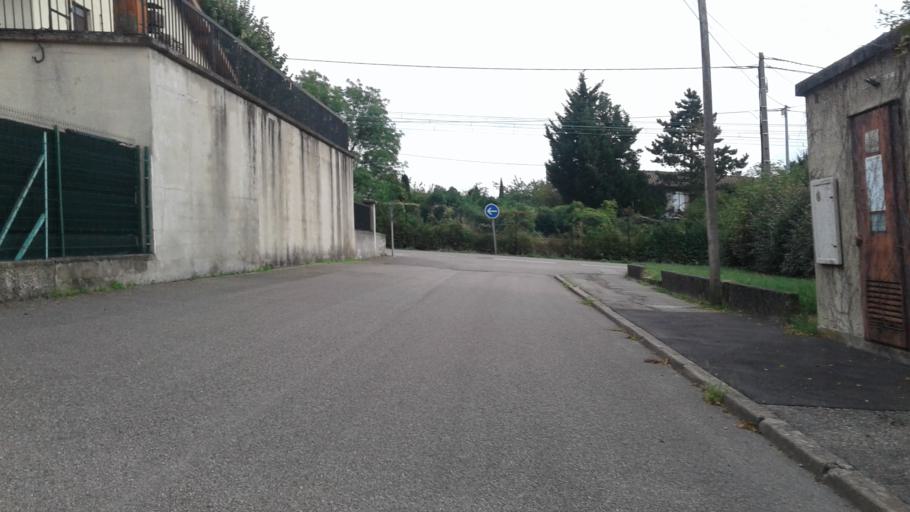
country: FR
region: Rhone-Alpes
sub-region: Departement de l'Ain
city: Beynost
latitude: 45.8336
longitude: 5.0036
